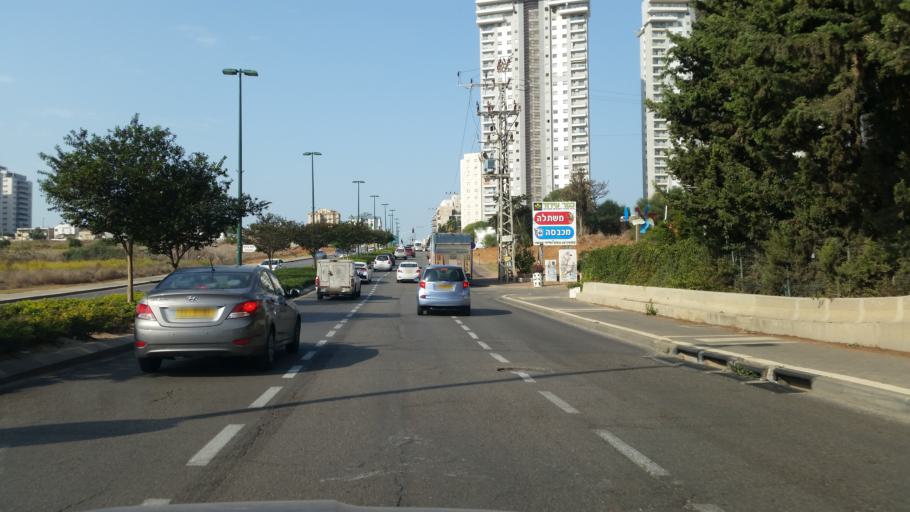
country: IL
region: Central District
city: Netanya
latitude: 32.3120
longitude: 34.8636
